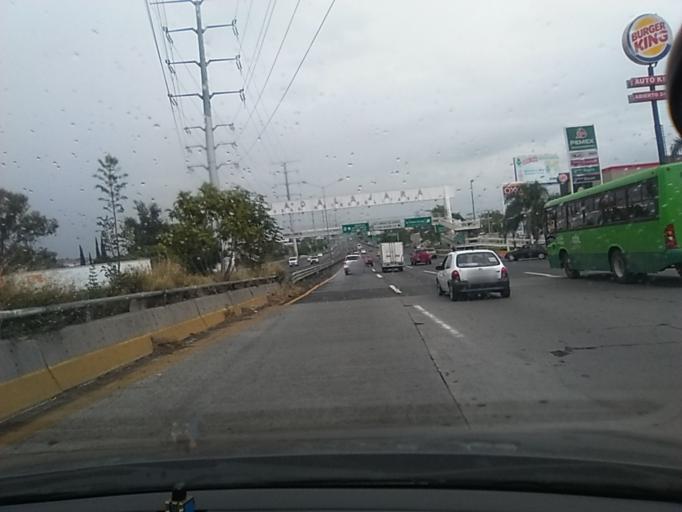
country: MX
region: Jalisco
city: Tlaquepaque
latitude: 20.6282
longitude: -103.2914
